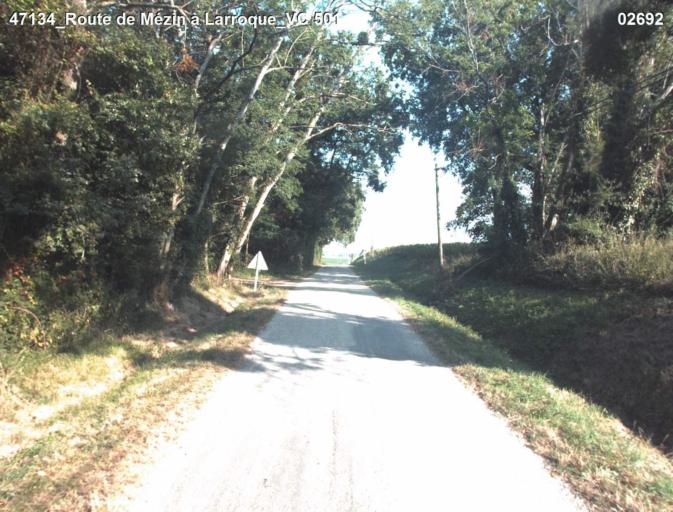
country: FR
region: Aquitaine
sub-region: Departement du Lot-et-Garonne
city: Mezin
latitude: 44.0197
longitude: 0.2722
